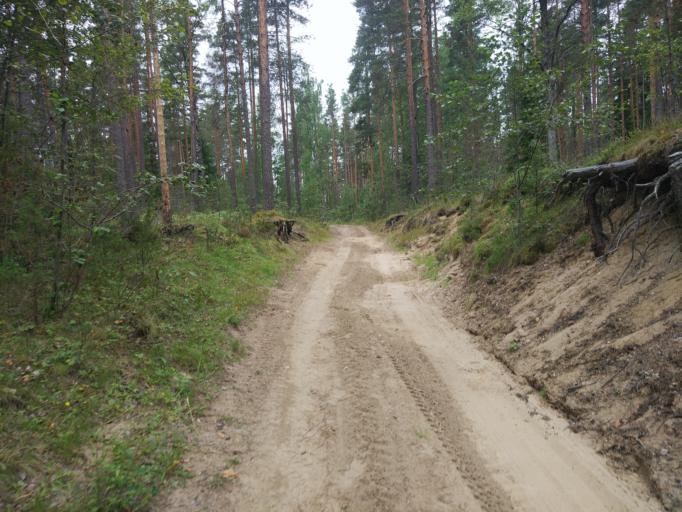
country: RU
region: Leningrad
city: Kuznechnoye
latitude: 61.0119
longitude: 29.6448
